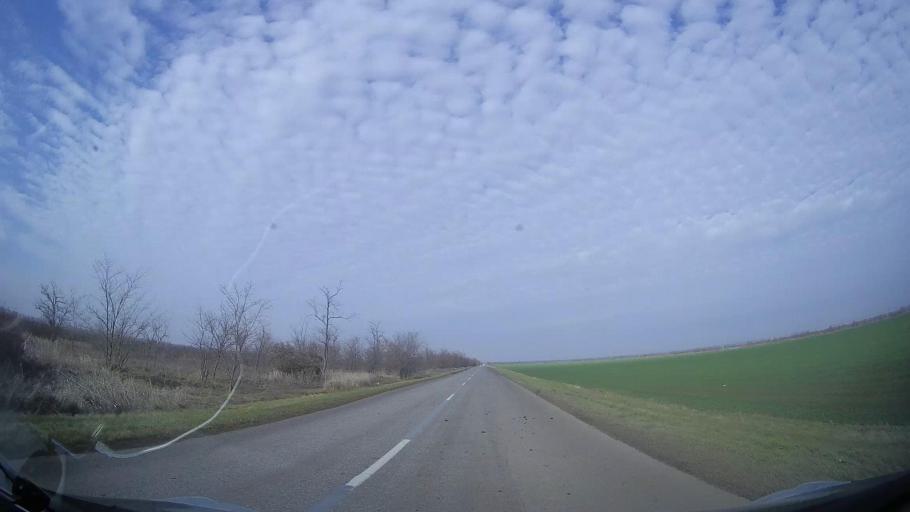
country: RU
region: Rostov
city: Gigant
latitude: 46.8614
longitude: 41.2794
